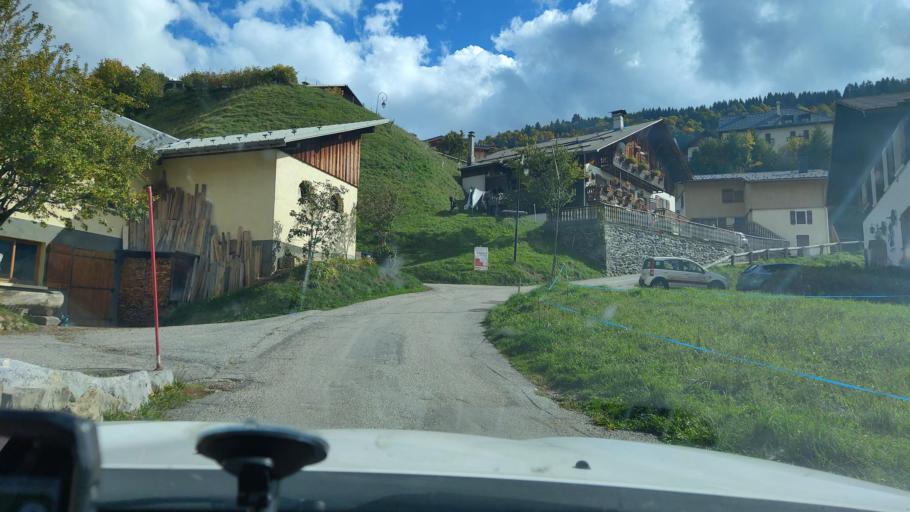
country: FR
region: Rhone-Alpes
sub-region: Departement de la Haute-Savoie
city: Praz-sur-Arly
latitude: 45.8192
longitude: 6.5130
